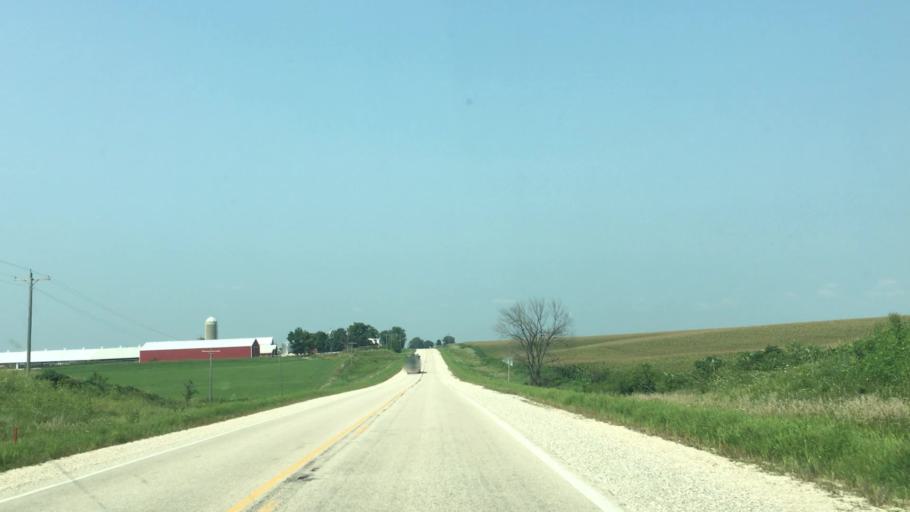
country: US
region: Iowa
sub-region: Fayette County
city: West Union
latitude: 43.0102
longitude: -91.8242
